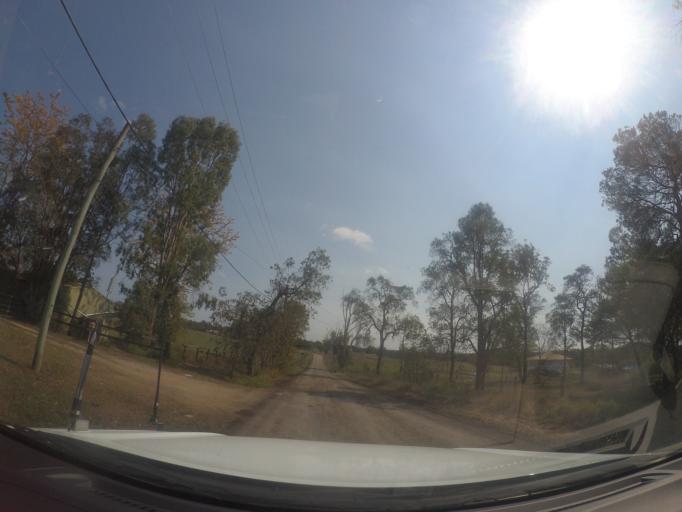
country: AU
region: Queensland
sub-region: Logan
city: Chambers Flat
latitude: -27.7605
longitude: 153.0591
